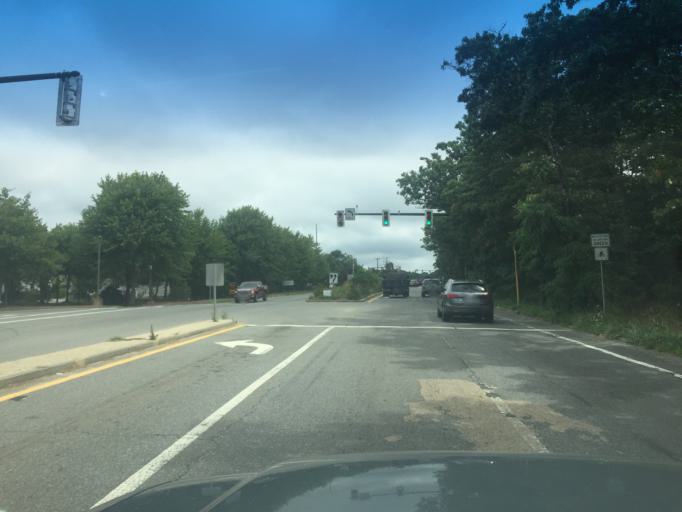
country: US
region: Massachusetts
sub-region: Barnstable County
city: Marstons Mills
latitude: 41.6474
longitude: -70.4266
